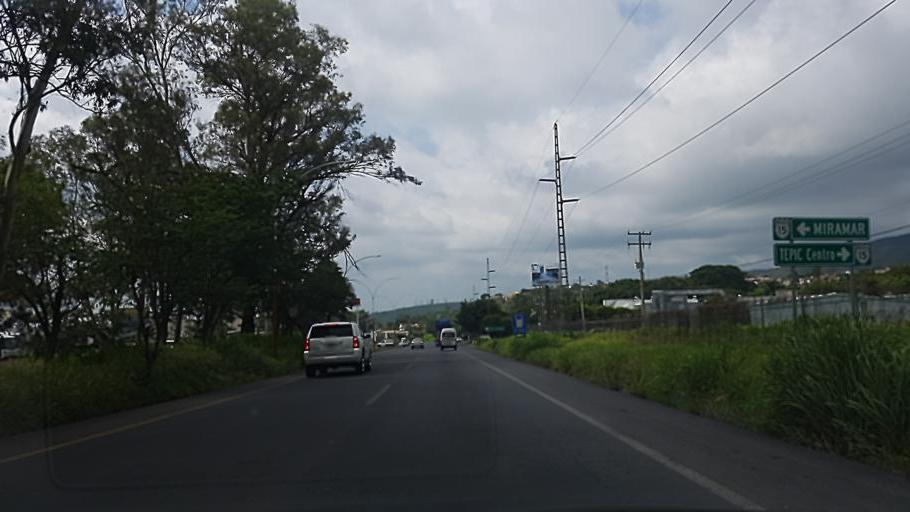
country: MX
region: Nayarit
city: Tepic
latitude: 21.5182
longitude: -104.9251
